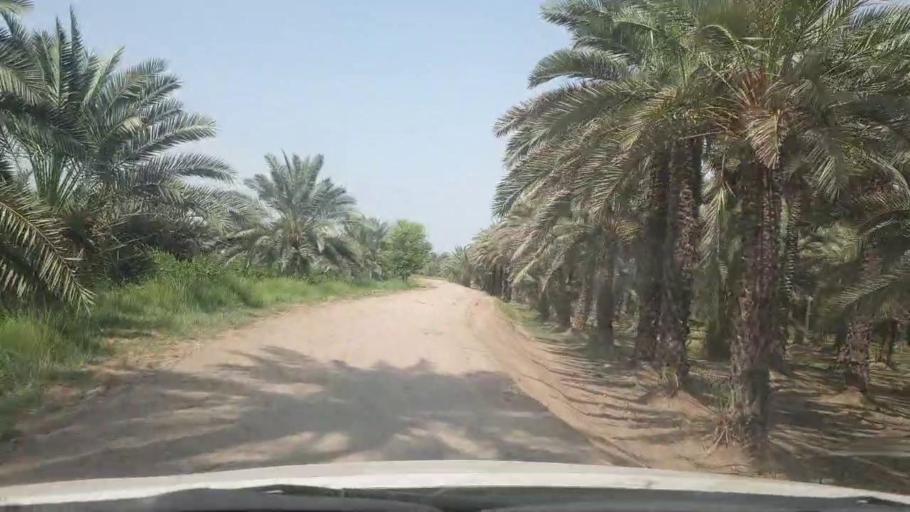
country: PK
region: Sindh
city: Khairpur
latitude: 27.5546
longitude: 68.8406
